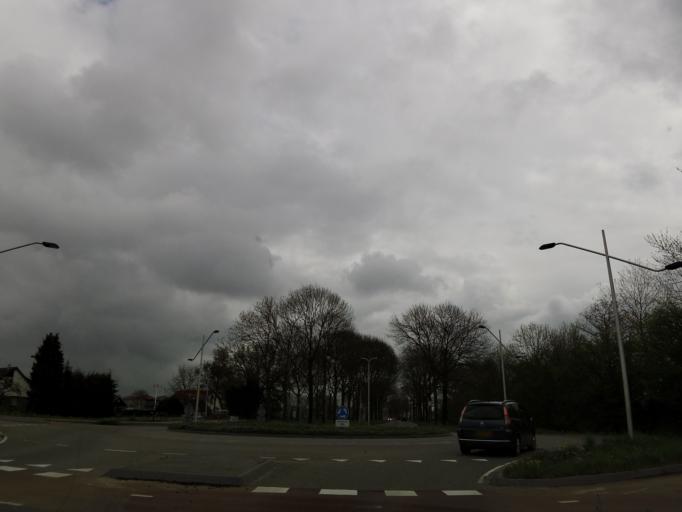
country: NL
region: Gelderland
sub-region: Gemeente Culemborg
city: Culemborg
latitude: 51.9435
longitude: 5.2008
